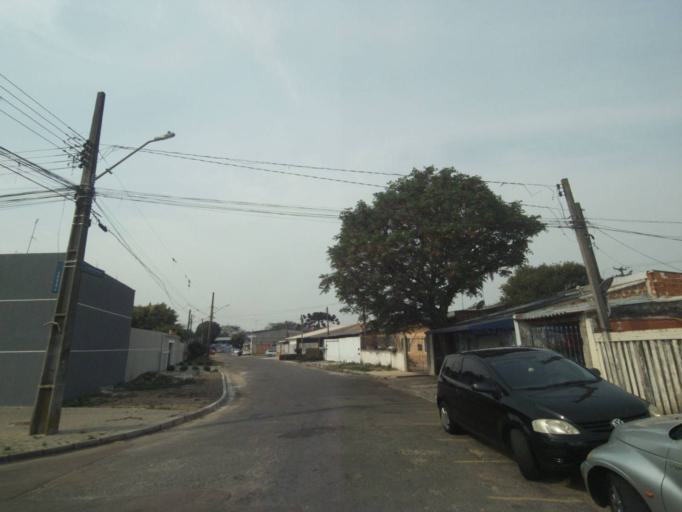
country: BR
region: Parana
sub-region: Sao Jose Dos Pinhais
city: Sao Jose dos Pinhais
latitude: -25.5284
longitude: -49.2706
